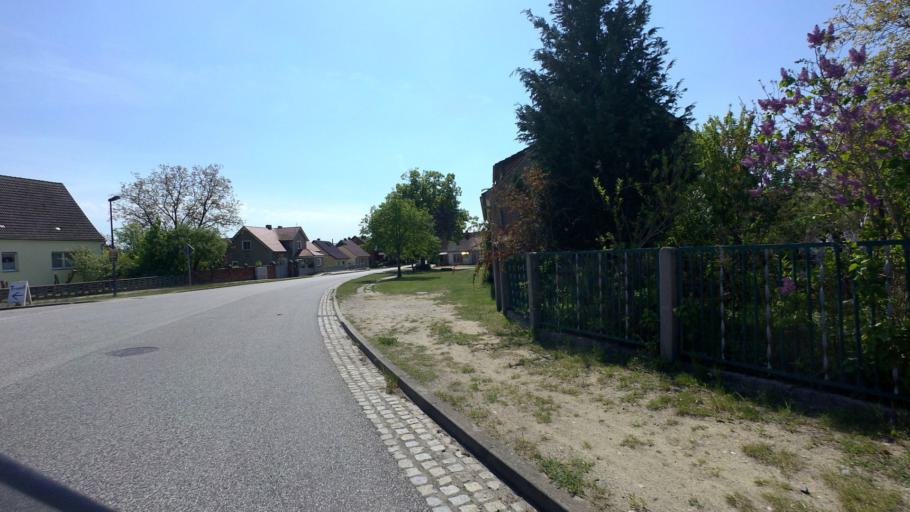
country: DE
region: Brandenburg
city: Neu Zauche
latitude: 52.0383
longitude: 14.0379
